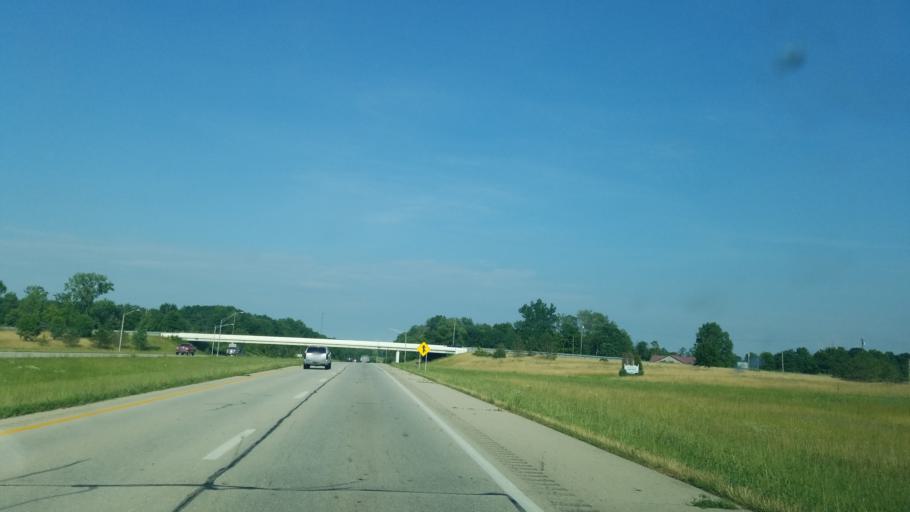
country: US
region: Ohio
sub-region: Clermont County
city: Williamsburg
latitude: 39.0671
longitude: -84.0631
